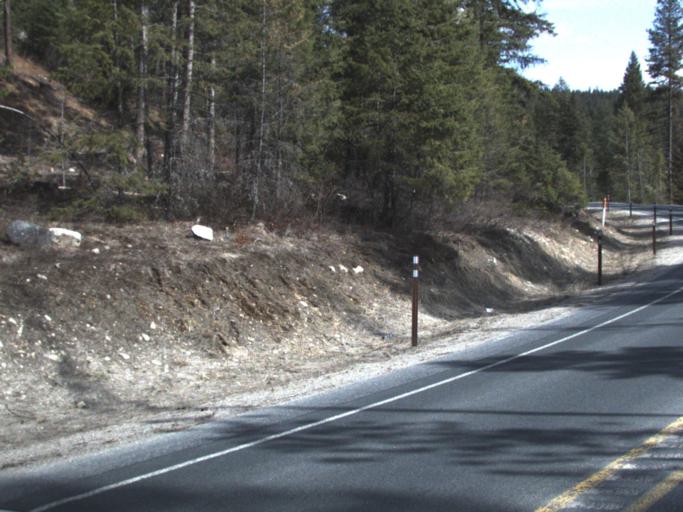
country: US
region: Washington
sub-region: Stevens County
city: Chewelah
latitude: 48.5060
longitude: -117.6650
